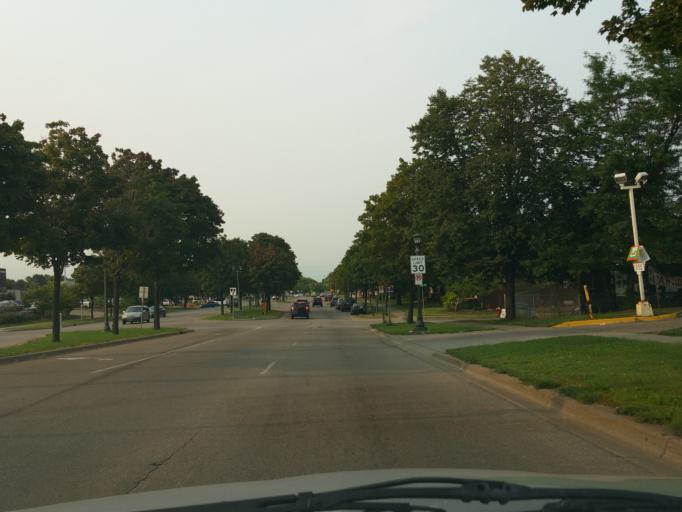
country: US
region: Minnesota
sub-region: Ramsey County
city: Falcon Heights
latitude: 44.9525
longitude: -93.1464
